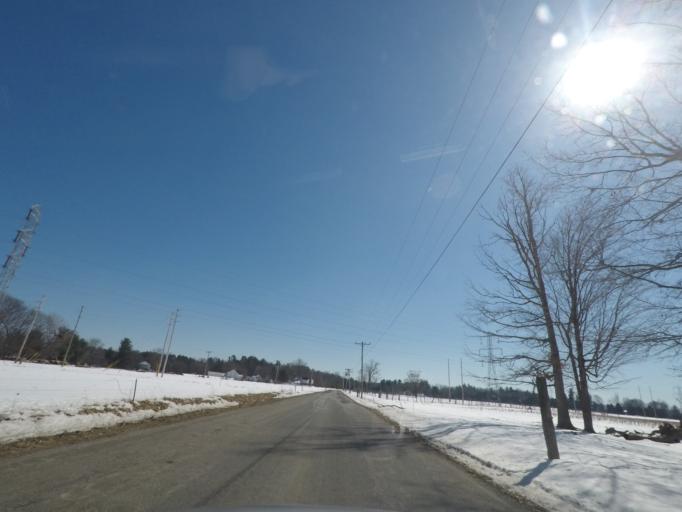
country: US
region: New York
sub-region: Saratoga County
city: Stillwater
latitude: 42.9120
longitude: -73.6095
